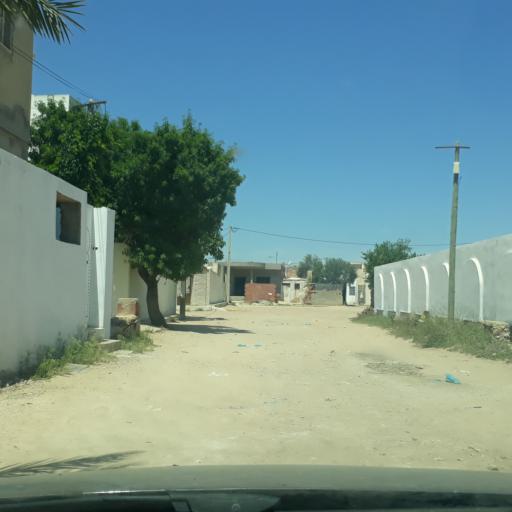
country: TN
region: Safaqis
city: Al Qarmadah
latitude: 34.8173
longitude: 10.7537
